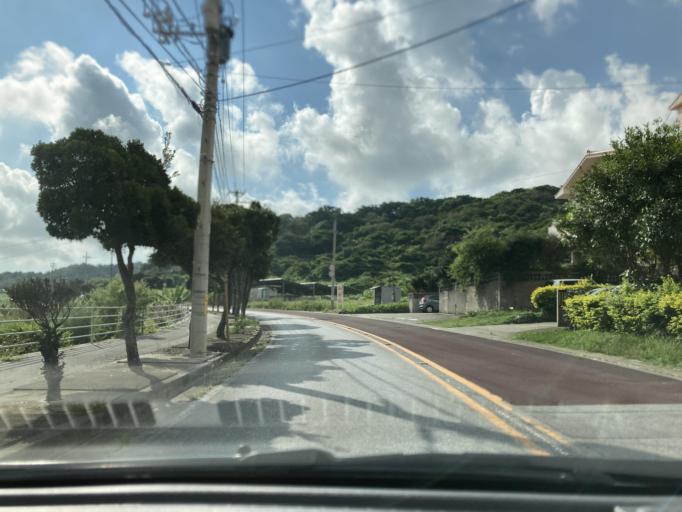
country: JP
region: Okinawa
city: Tomigusuku
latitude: 26.1502
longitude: 127.7530
